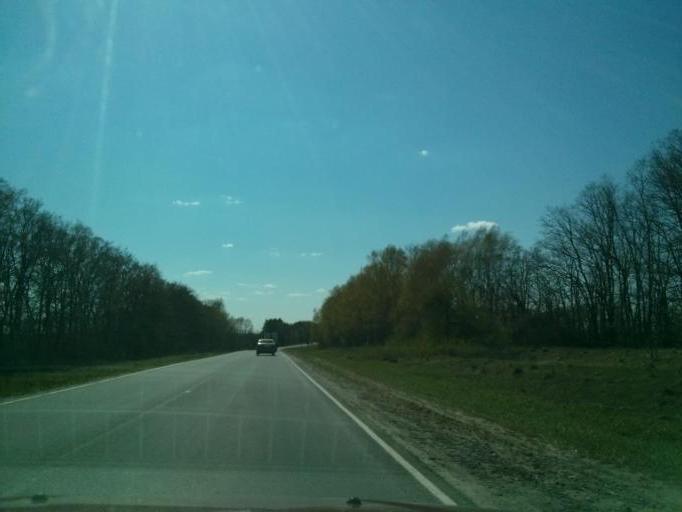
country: RU
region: Nizjnij Novgorod
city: Bogorodsk
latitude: 56.0537
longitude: 43.4076
